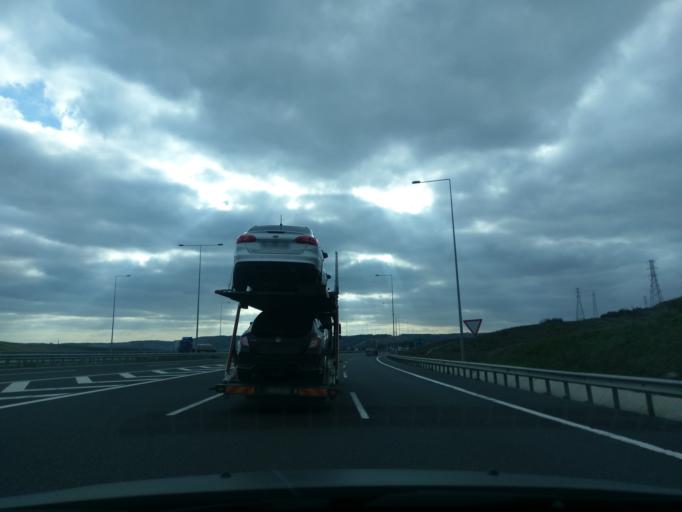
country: TR
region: Istanbul
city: Kemerburgaz
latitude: 41.2265
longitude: 28.8418
